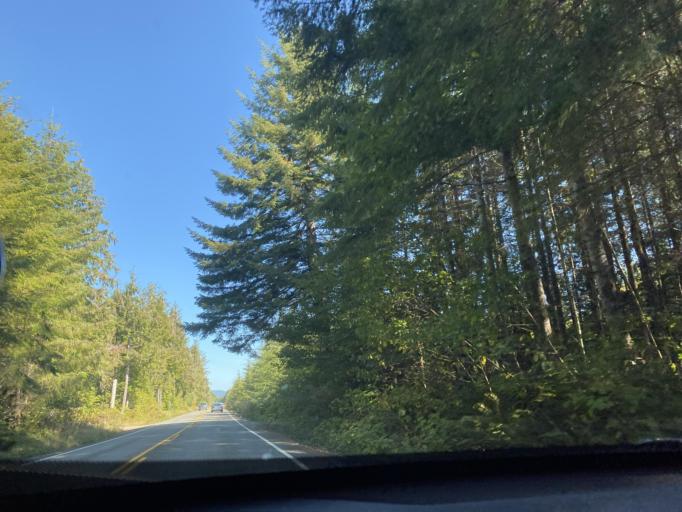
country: US
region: Washington
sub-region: Clallam County
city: Forks
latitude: 47.9236
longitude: -124.4986
